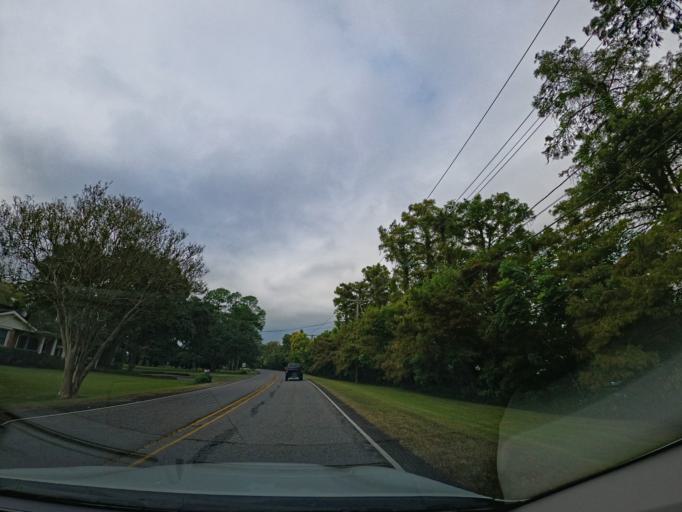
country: US
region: Louisiana
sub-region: Terrebonne Parish
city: Houma
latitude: 29.5770
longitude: -90.7373
